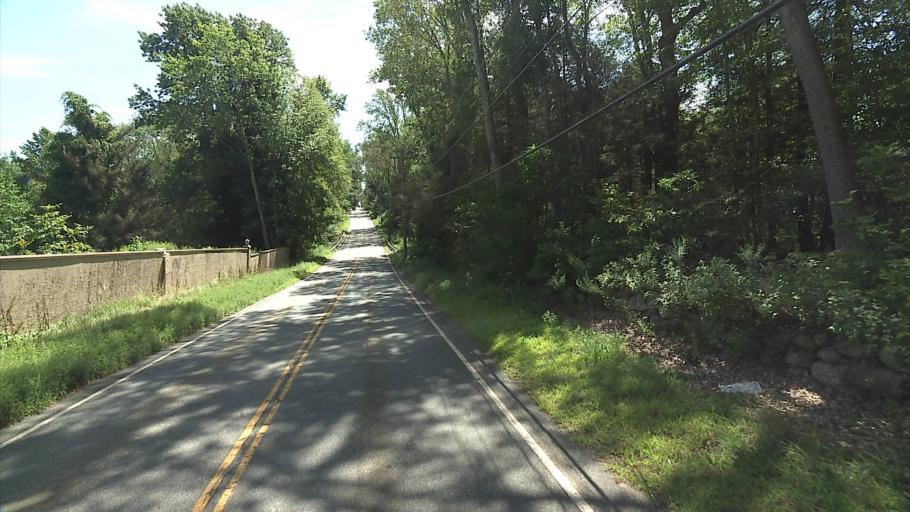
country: US
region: Connecticut
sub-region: Windham County
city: South Woodstock
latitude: 41.8798
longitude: -71.9753
